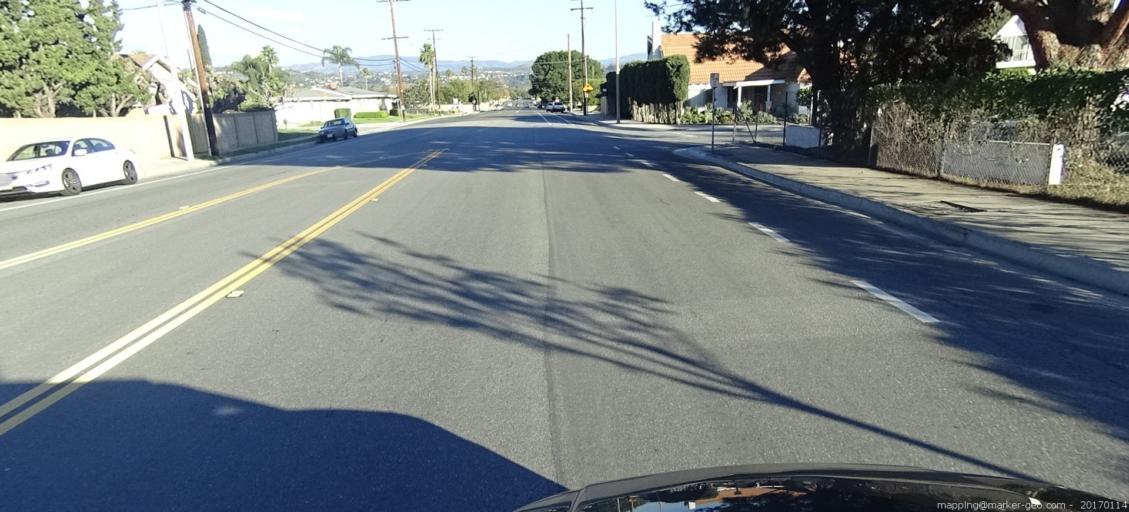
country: US
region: California
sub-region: Orange County
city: Tustin
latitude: 33.7671
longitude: -117.8291
